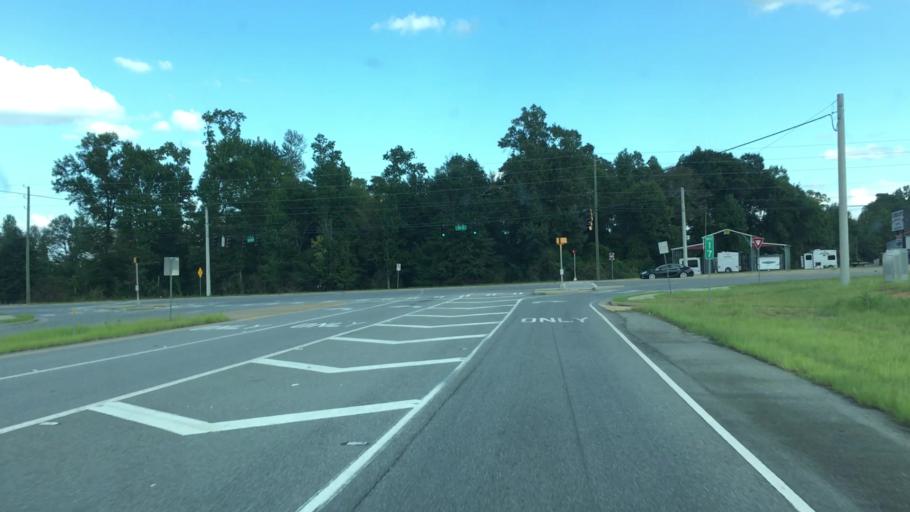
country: US
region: Georgia
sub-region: Laurens County
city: Dublin
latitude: 32.4995
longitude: -82.9280
